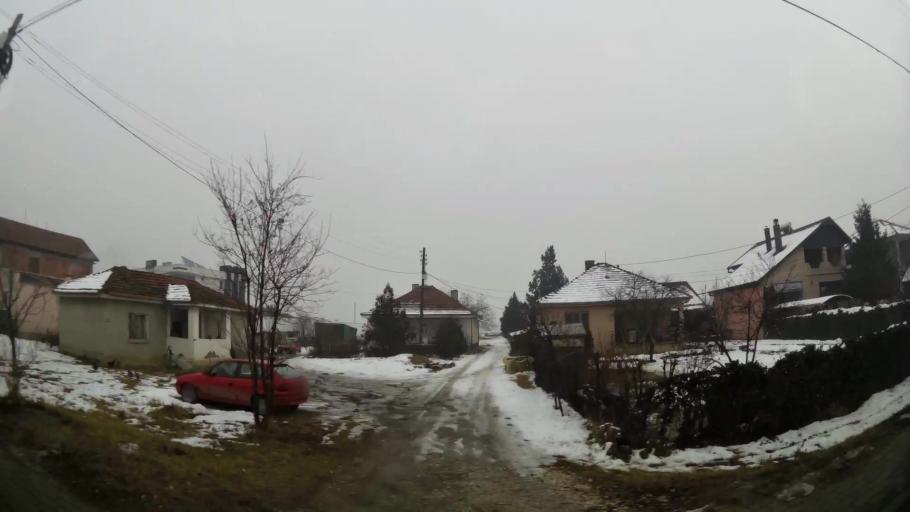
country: MK
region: Petrovec
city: Petrovec
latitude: 41.9388
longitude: 21.6188
